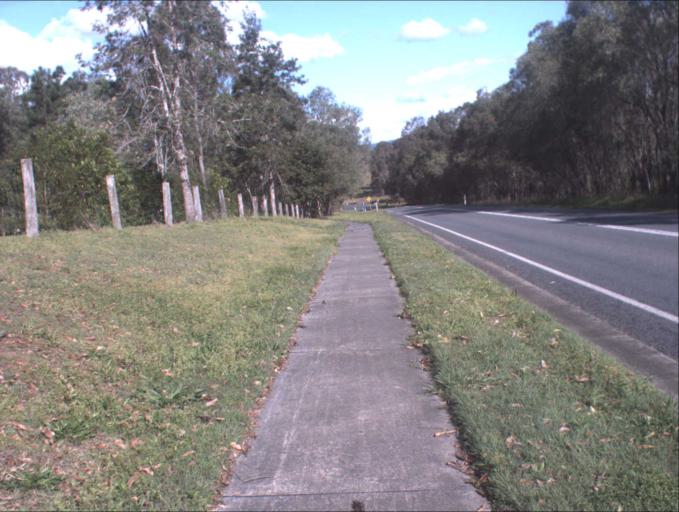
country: AU
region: Queensland
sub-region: Logan
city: Chambers Flat
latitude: -27.7615
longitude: 153.0918
